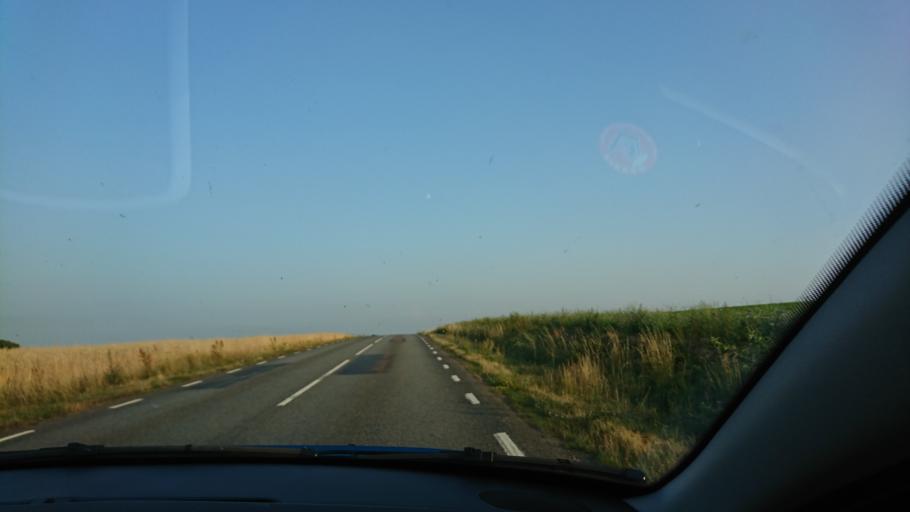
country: SE
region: Skane
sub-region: Simrishamns Kommun
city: Kivik
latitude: 55.6975
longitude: 14.1539
